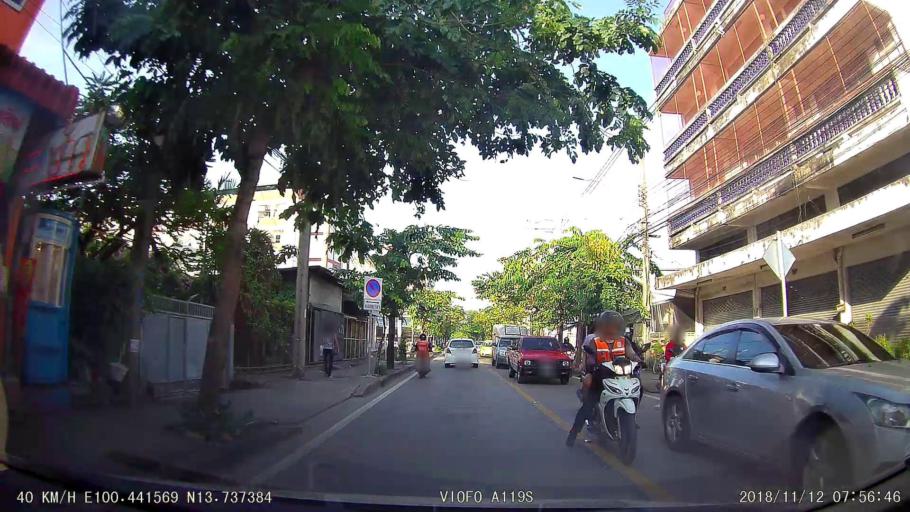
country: TH
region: Bangkok
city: Phasi Charoen
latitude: 13.7374
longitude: 100.4415
